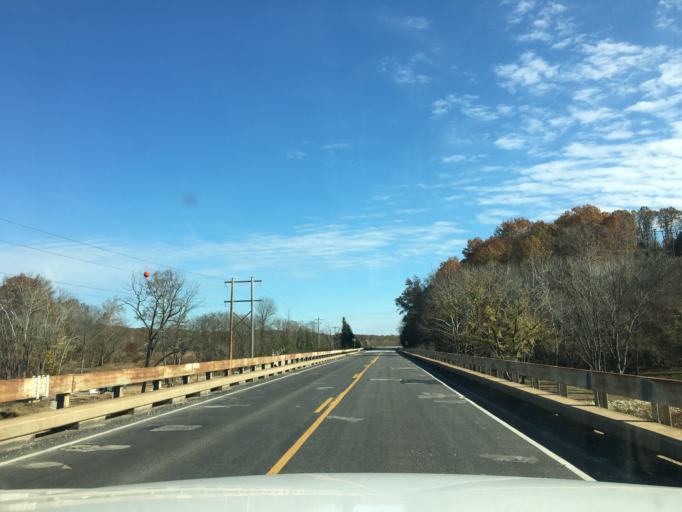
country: US
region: Missouri
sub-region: Osage County
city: Linn
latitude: 38.3888
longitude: -91.8206
